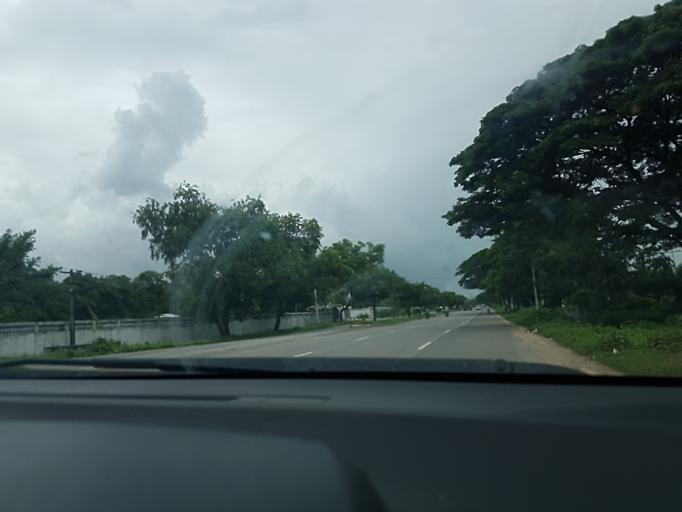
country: MM
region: Bago
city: Thanatpin
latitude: 17.1463
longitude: 96.3125
